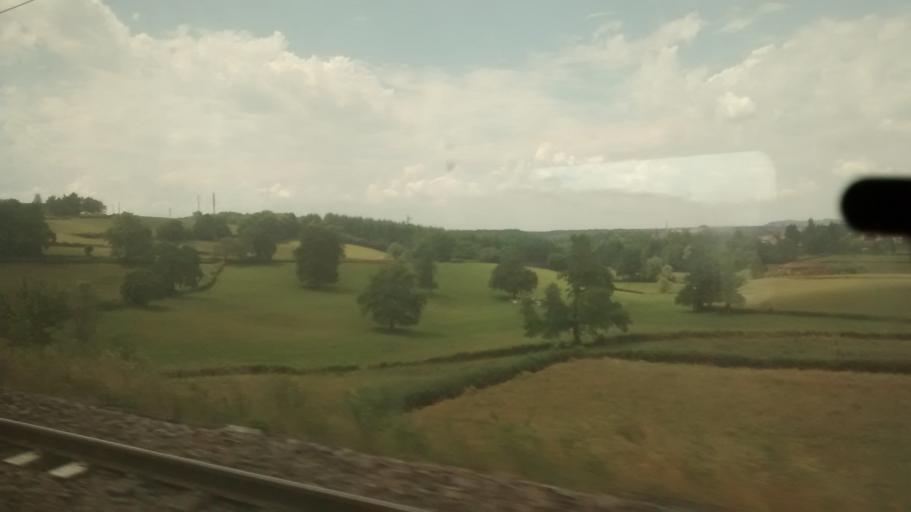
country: FR
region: Bourgogne
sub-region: Departement de Saone-et-Loire
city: Le Breuil
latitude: 46.8001
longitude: 4.4959
